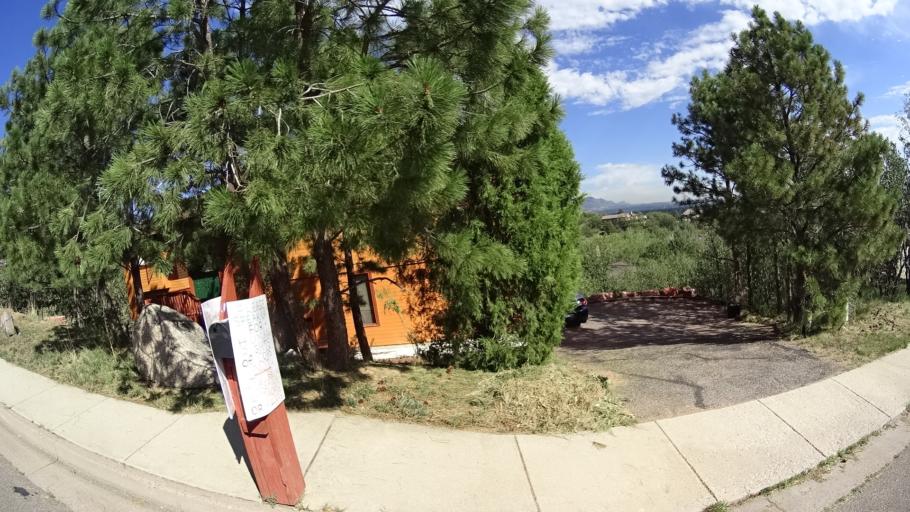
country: US
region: Colorado
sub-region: El Paso County
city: Stratmoor
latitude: 38.7659
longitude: -104.8236
